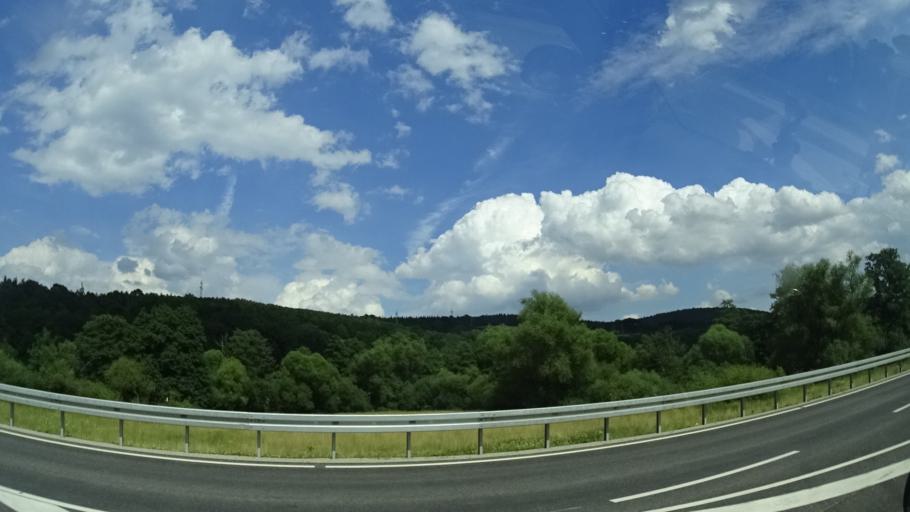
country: DE
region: Hesse
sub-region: Regierungsbezirk Kassel
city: Bad Hersfeld
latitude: 50.8243
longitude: 9.7286
